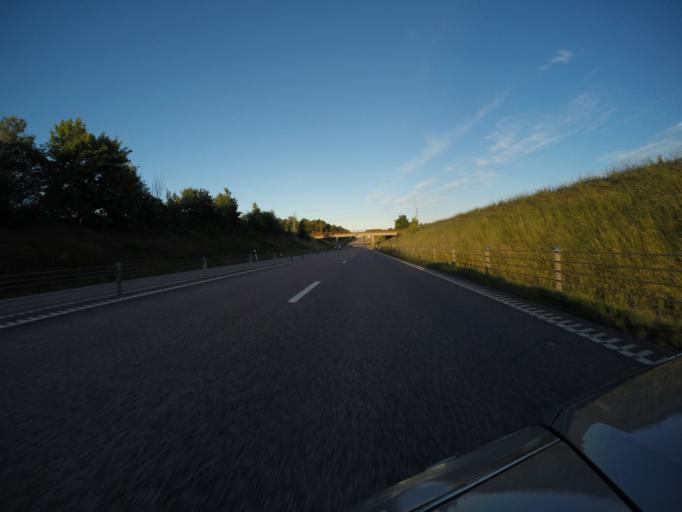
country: SE
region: Skane
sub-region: Bjuvs Kommun
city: Bjuv
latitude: 56.0782
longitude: 12.8986
